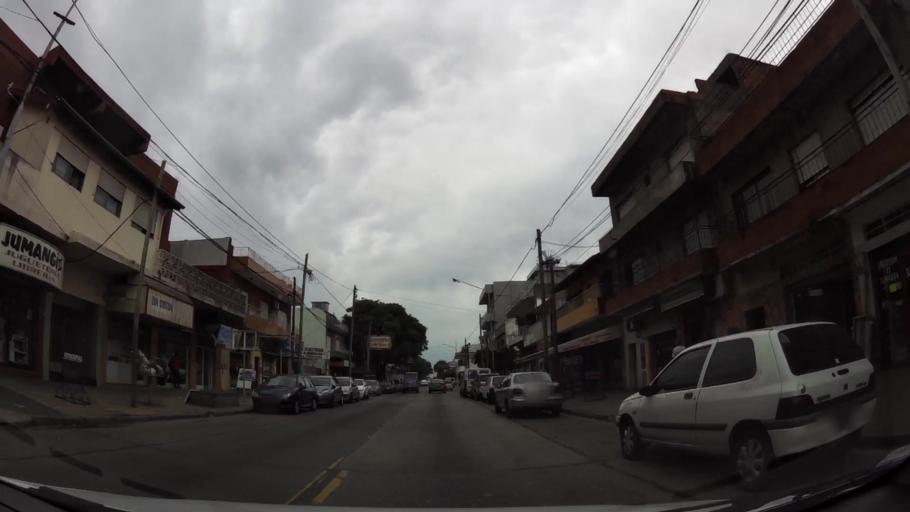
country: AR
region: Buenos Aires
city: San Justo
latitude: -34.6719
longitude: -58.5303
